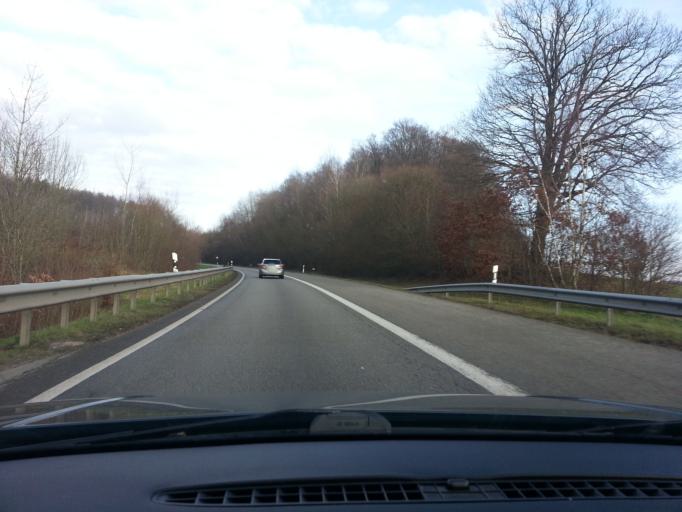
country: DE
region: Rheinland-Pfalz
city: Hoheischweiler
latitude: 49.2220
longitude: 7.5488
